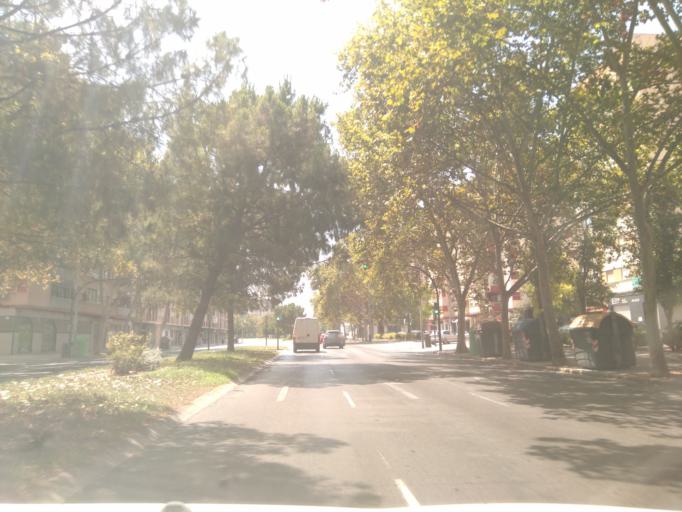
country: ES
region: Valencia
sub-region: Provincia de Valencia
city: Mislata
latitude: 39.4847
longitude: -0.3988
